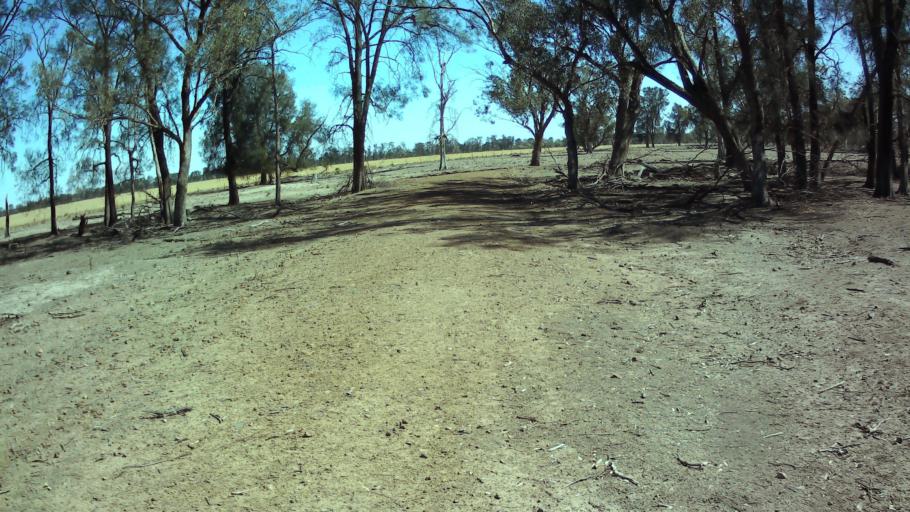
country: AU
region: New South Wales
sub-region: Bland
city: West Wyalong
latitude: -33.7689
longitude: 147.6570
